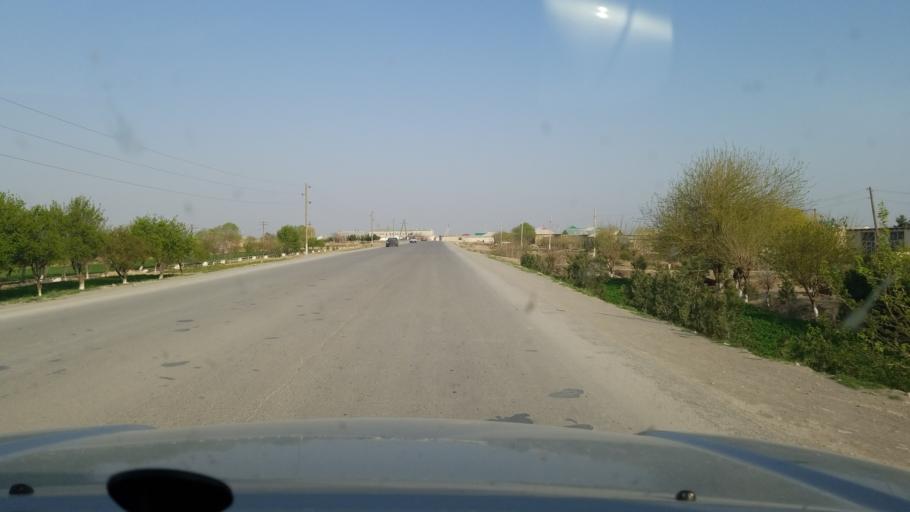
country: AF
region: Jowzjan
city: Qarqin
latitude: 37.5156
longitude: 65.9804
